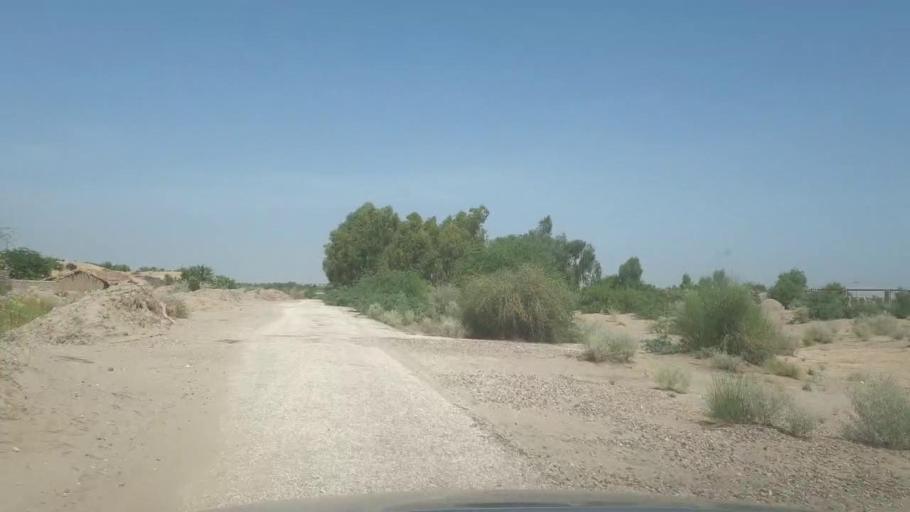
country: PK
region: Sindh
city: Khairpur
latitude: 27.3955
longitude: 69.0729
